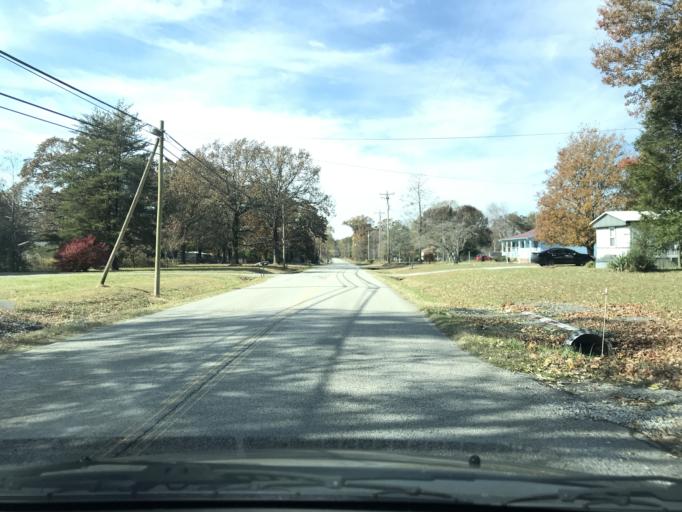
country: US
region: Tennessee
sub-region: Coffee County
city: Tullahoma
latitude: 35.3897
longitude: -86.1613
